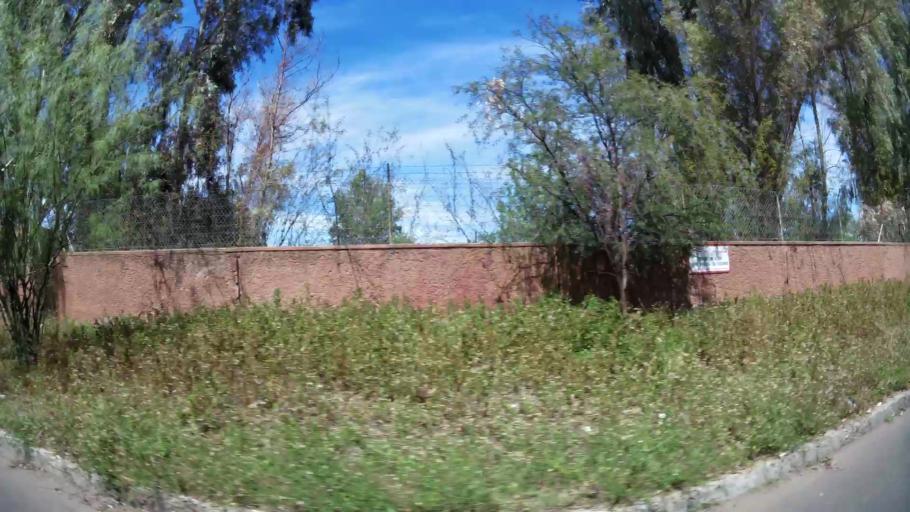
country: MA
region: Marrakech-Tensift-Al Haouz
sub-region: Marrakech
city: Marrakesh
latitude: 31.6441
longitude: -8.0559
